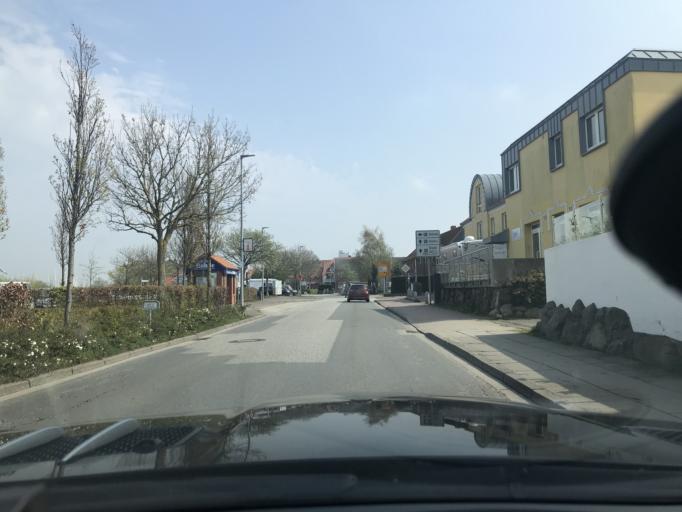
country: DE
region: Schleswig-Holstein
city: Heiligenhafen
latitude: 54.3743
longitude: 10.9775
